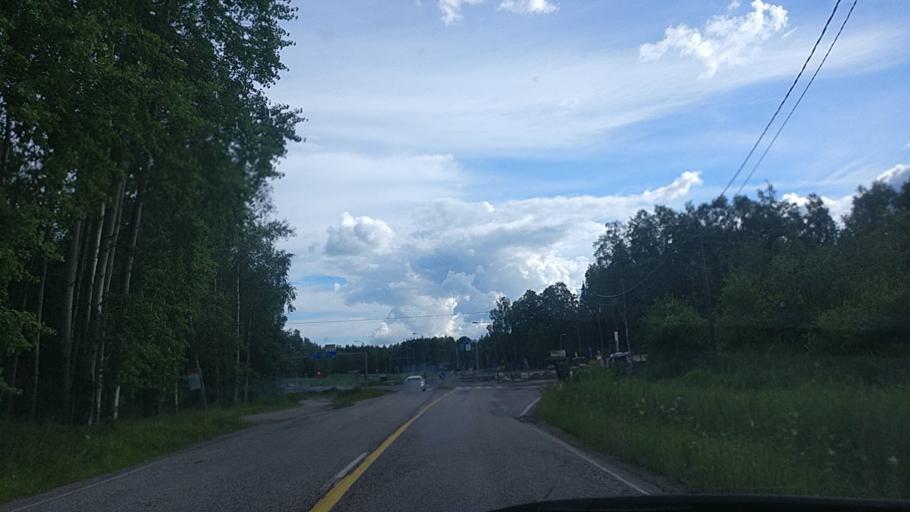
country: FI
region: Uusimaa
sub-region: Helsinki
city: Kauniainen
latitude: 60.3181
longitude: 24.7165
